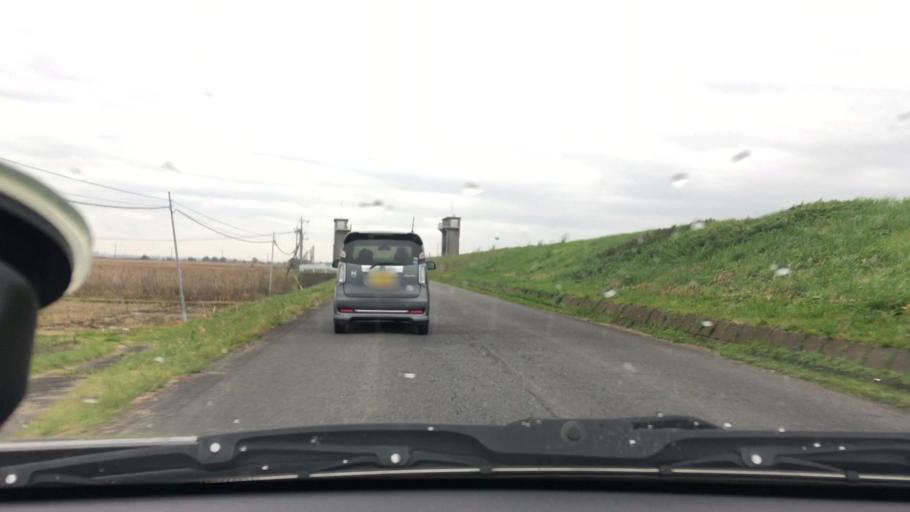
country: JP
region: Chiba
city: Omigawa
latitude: 35.8674
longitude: 140.6225
